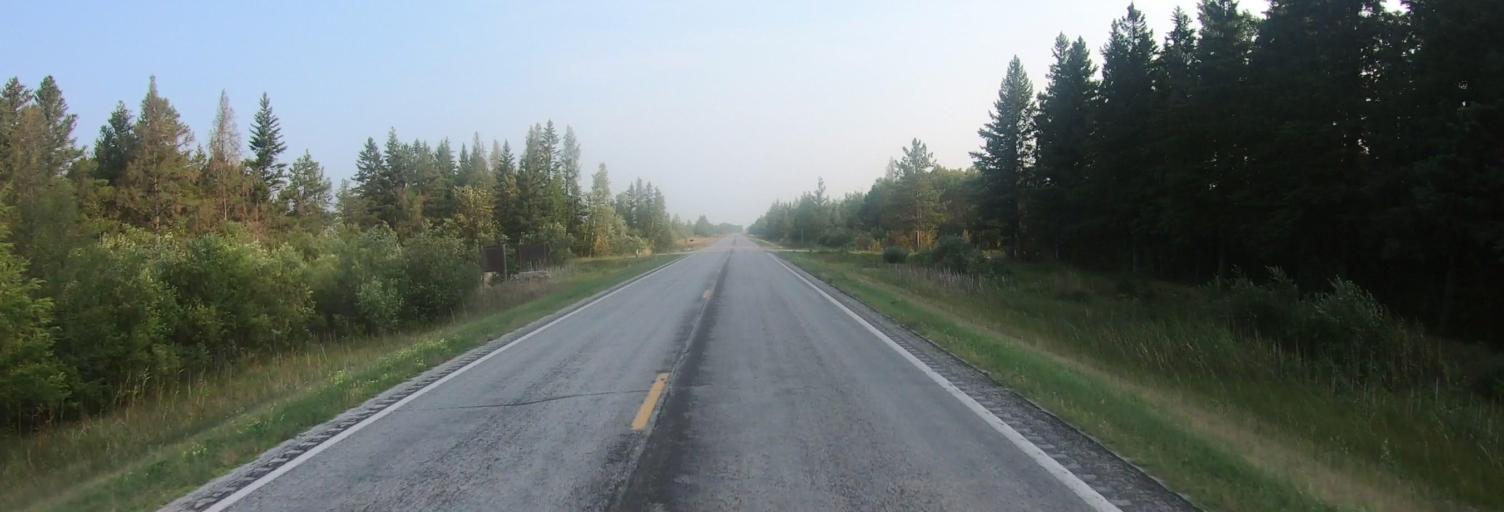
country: US
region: Minnesota
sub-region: Roseau County
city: Warroad
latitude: 48.7557
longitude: -95.3305
